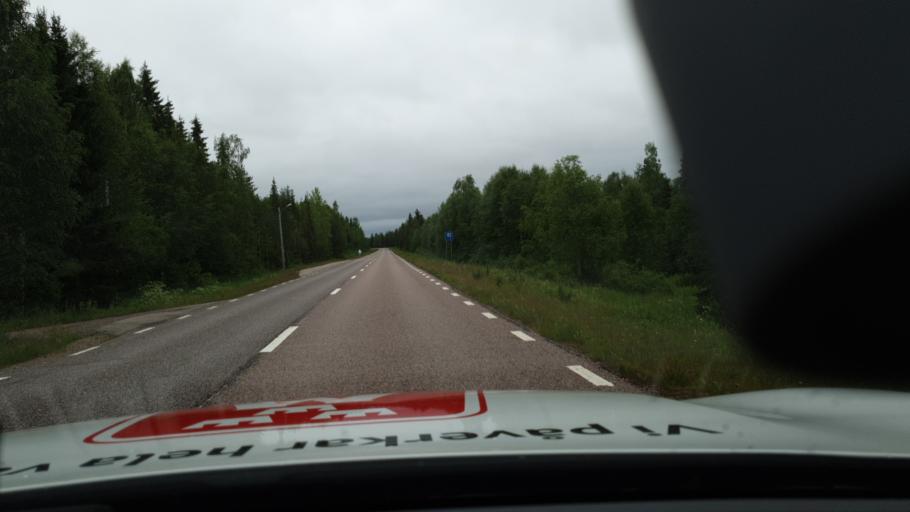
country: FI
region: Lapland
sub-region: Tunturi-Lappi
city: Kolari
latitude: 67.0791
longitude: 23.6605
